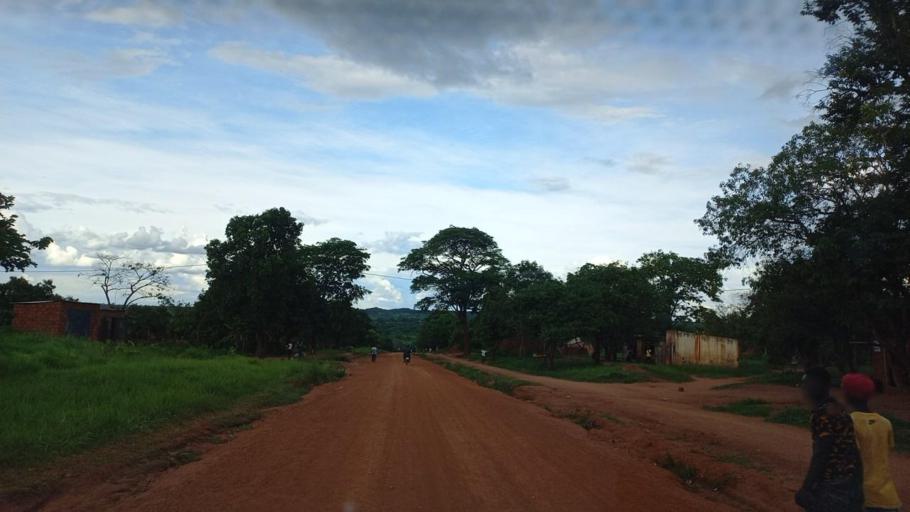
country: ZM
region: North-Western
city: Mwinilunga
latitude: -11.7582
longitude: 24.4297
